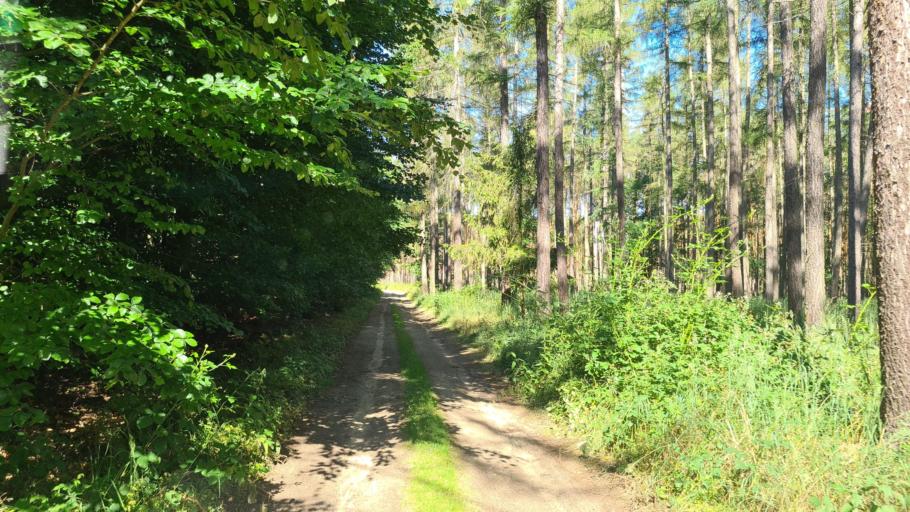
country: DE
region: Brandenburg
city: Treuenbrietzen
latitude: 52.0148
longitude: 12.8532
